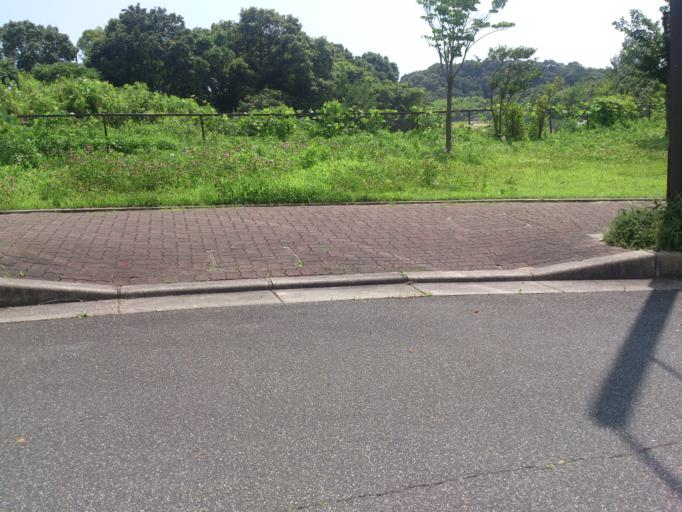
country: JP
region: Hyogo
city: Kobe
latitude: 34.7084
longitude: 135.1128
